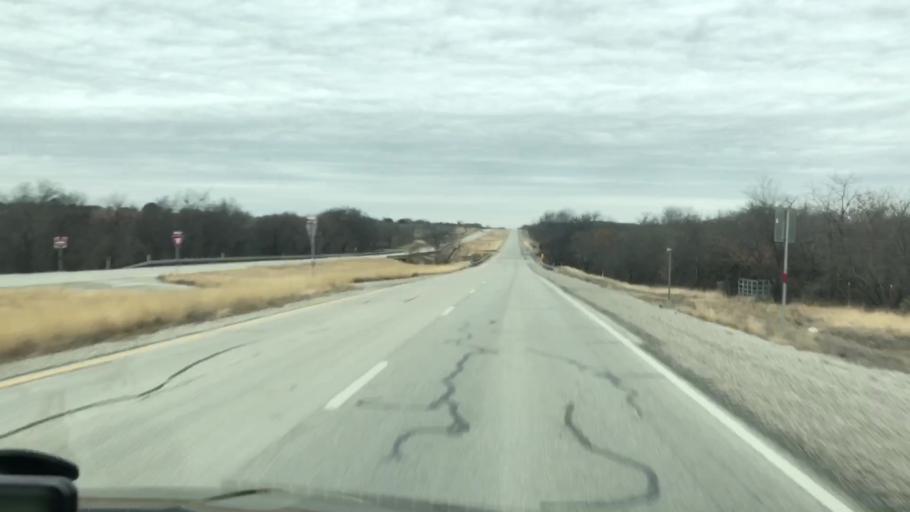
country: US
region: Texas
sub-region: Jack County
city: Jacksboro
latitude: 33.2398
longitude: -98.2160
